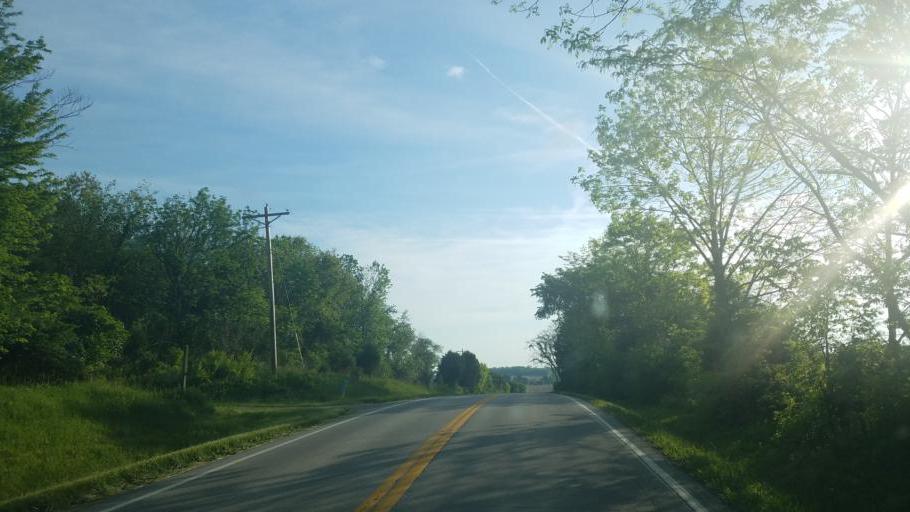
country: US
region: Ohio
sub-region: Highland County
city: Greenfield
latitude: 39.4059
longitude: -83.2999
